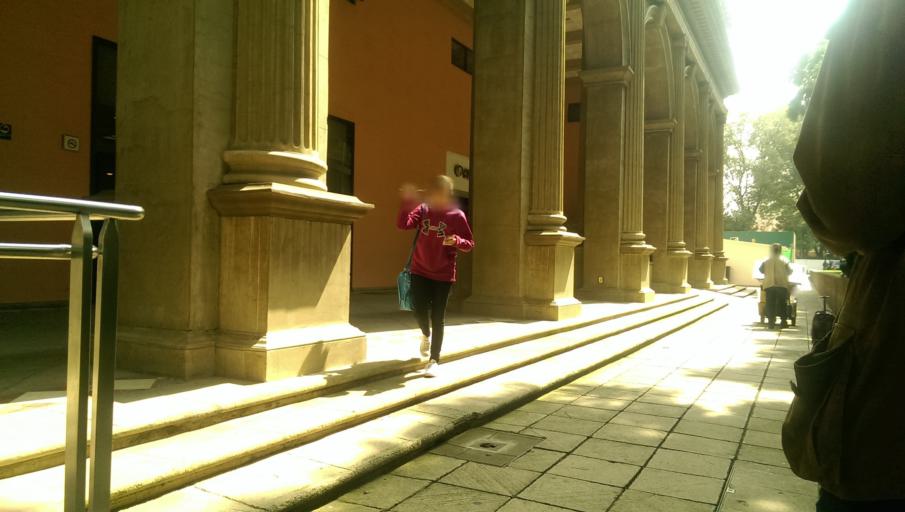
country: MX
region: Mexico City
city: Tlalpan
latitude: 19.2840
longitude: -99.1355
